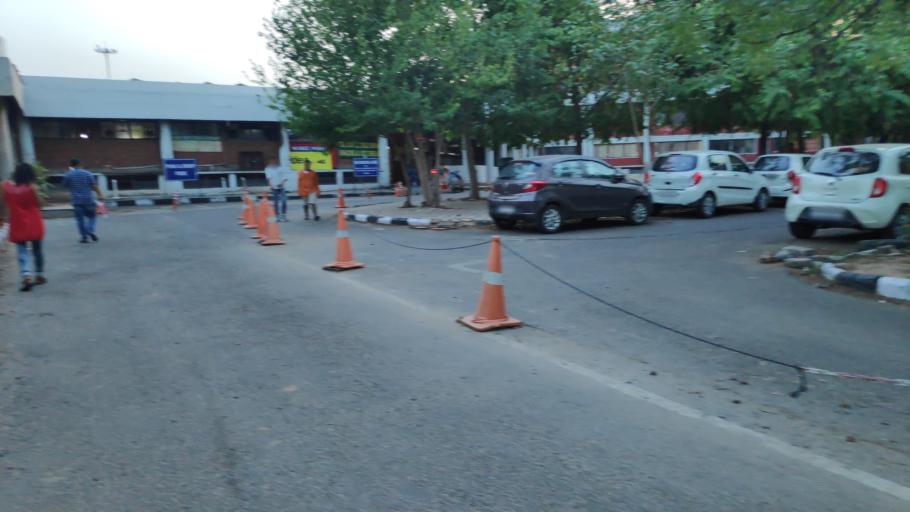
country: IN
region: Punjab
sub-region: Ajitgarh
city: Mohali
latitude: 30.7162
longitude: 76.7454
